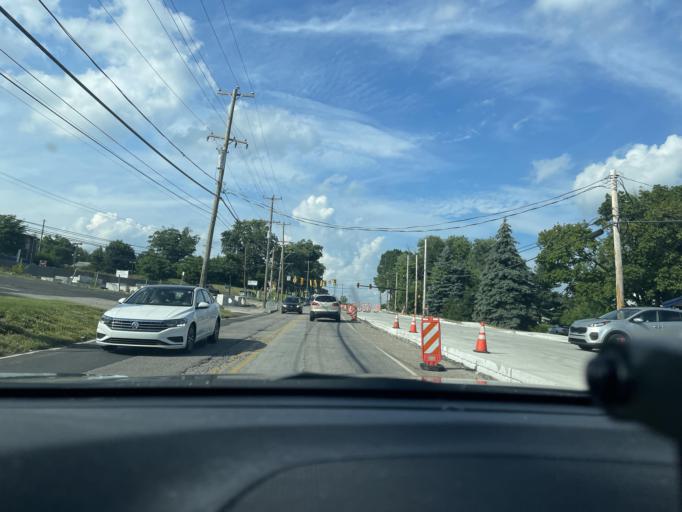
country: US
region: Pennsylvania
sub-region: Montgomery County
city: Blue Bell
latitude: 40.1512
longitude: -75.3058
